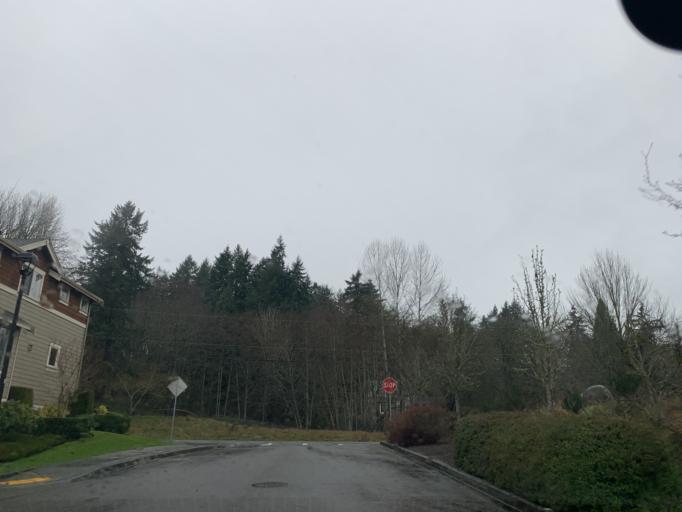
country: US
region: Washington
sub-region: King County
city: Woodinville
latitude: 47.7384
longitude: -122.1631
